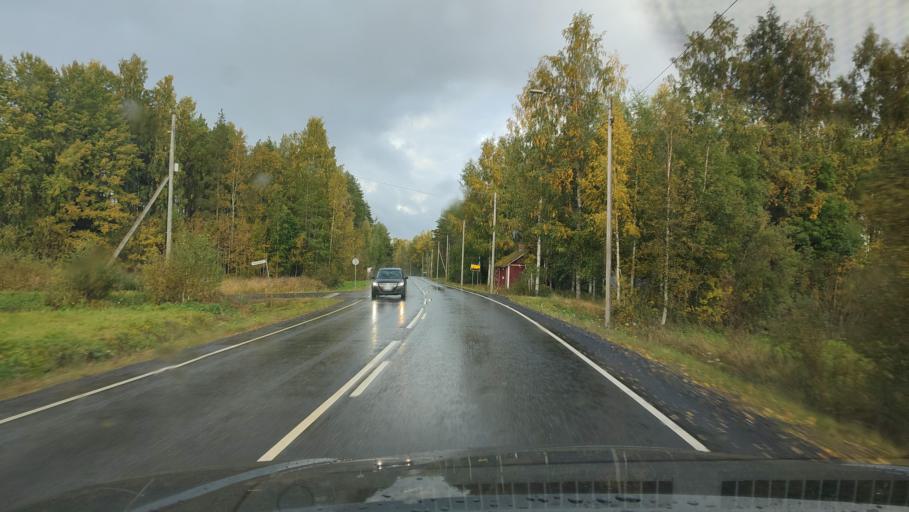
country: FI
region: Southern Ostrobothnia
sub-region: Suupohja
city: Karijoki
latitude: 62.3017
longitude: 21.6865
